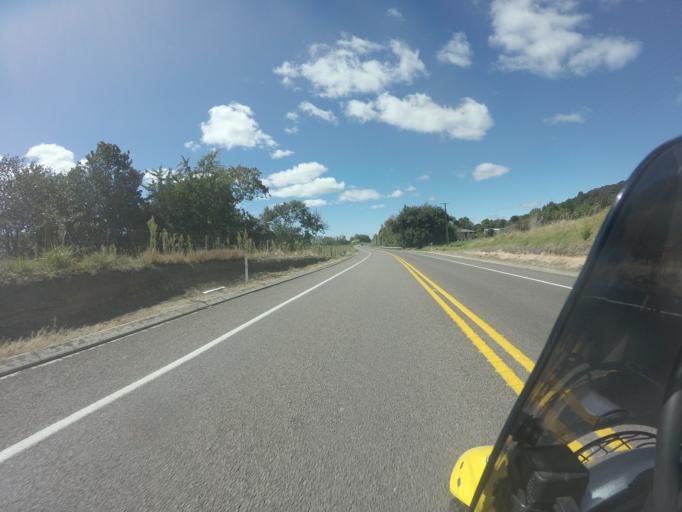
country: NZ
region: Bay of Plenty
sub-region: Whakatane District
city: Edgecumbe
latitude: -37.9979
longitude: 176.8753
